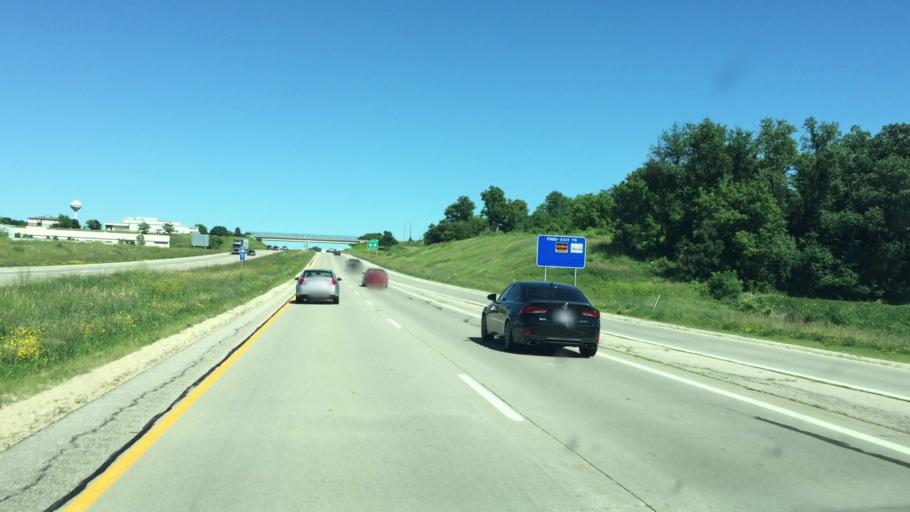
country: US
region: Wisconsin
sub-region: Dane County
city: Verona
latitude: 42.9740
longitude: -89.5414
